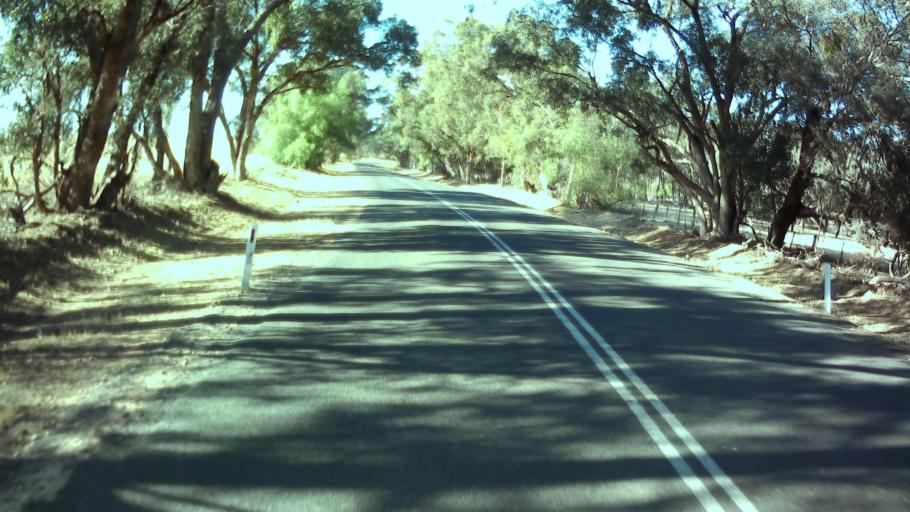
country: AU
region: New South Wales
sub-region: Weddin
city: Grenfell
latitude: -33.9955
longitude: 148.1325
